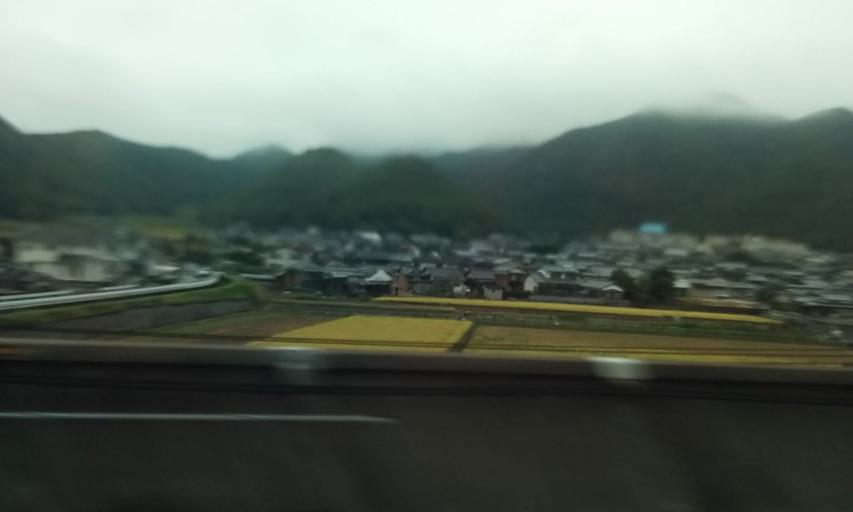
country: JP
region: Okayama
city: Okayama-shi
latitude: 34.7285
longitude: 134.1170
